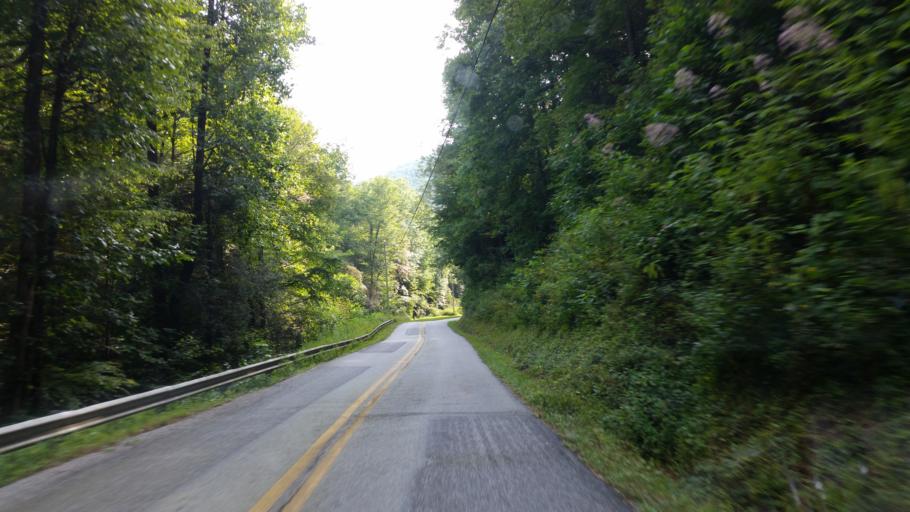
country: US
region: Georgia
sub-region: Lumpkin County
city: Dahlonega
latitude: 34.6763
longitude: -84.0261
